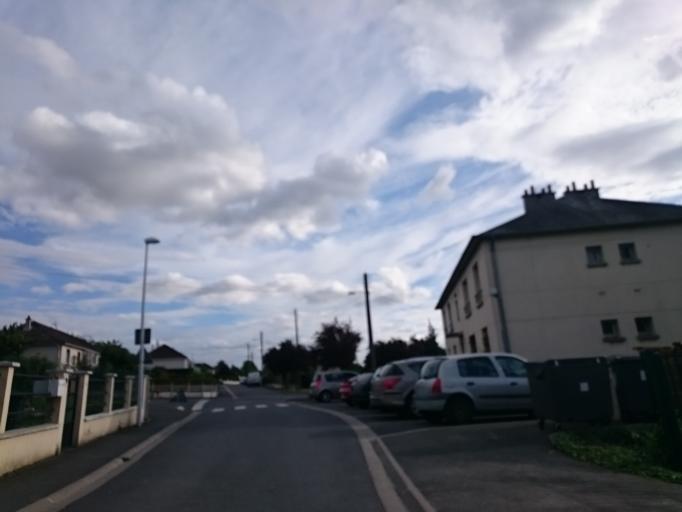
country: FR
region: Lower Normandy
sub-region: Departement du Calvados
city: Fleury-sur-Orne
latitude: 49.1464
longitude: -0.3772
